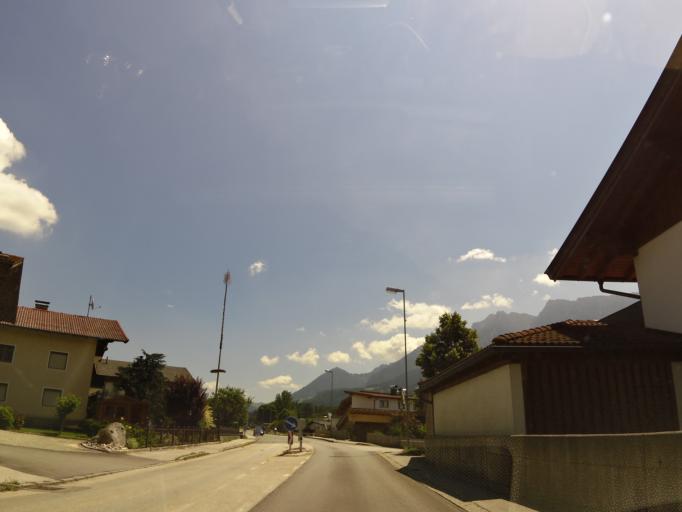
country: AT
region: Tyrol
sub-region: Politischer Bezirk Kufstein
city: Niederndorf
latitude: 47.6495
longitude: 12.2178
